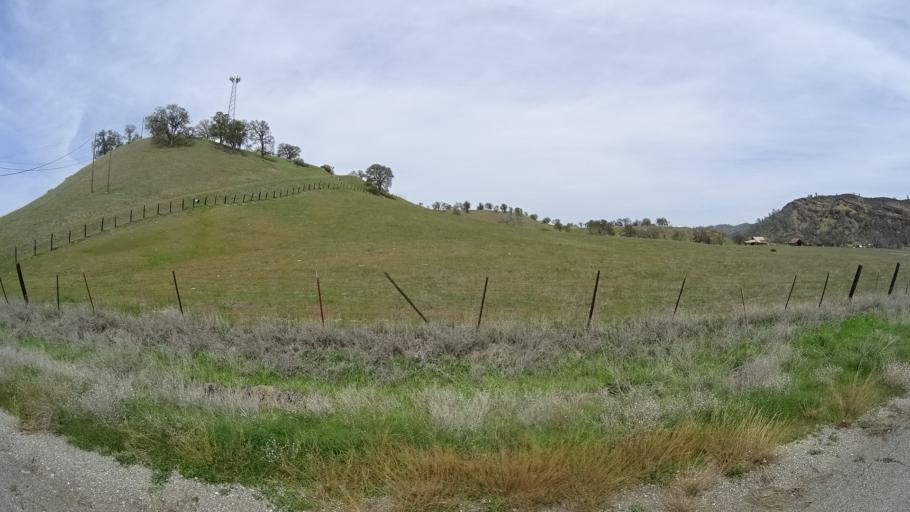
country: US
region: California
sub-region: Glenn County
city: Willows
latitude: 39.5945
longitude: -122.5465
